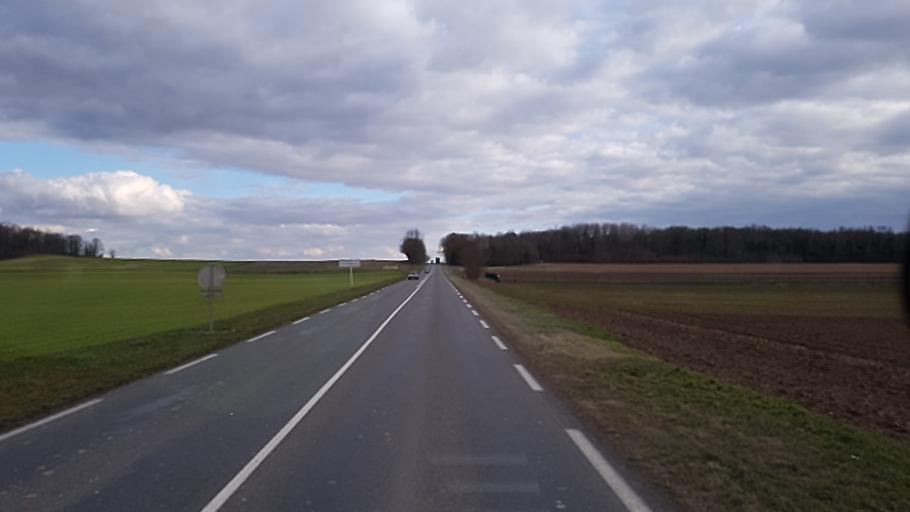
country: FR
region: Picardie
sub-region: Departement de l'Aisne
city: Saint-Erme-Outre-et-Ramecourt
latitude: 49.4582
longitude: 3.8295
